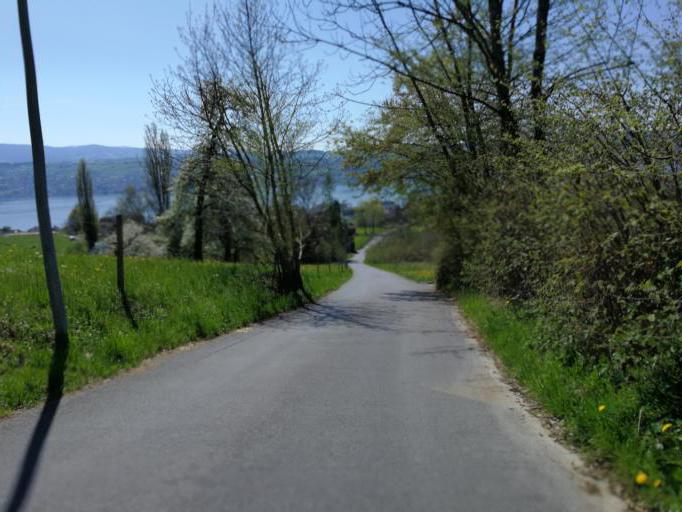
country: CH
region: Zurich
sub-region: Bezirk Meilen
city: Maennedorf / Dorfkern
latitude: 47.2653
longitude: 8.6936
